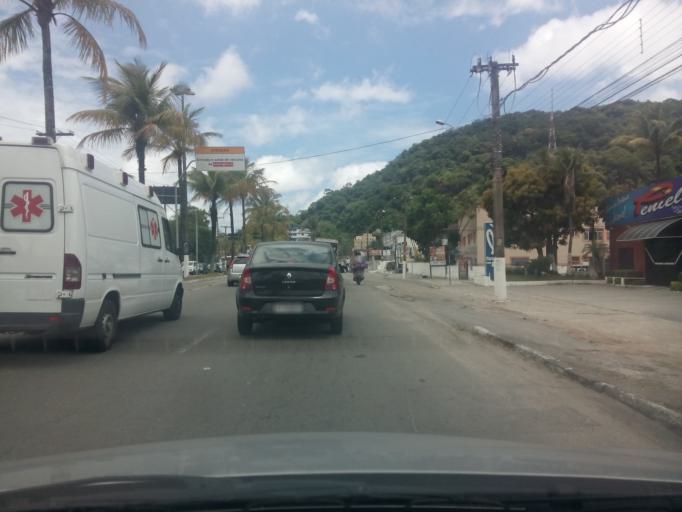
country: BR
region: Sao Paulo
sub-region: Guaruja
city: Guaruja
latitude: -23.9870
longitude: -46.2651
